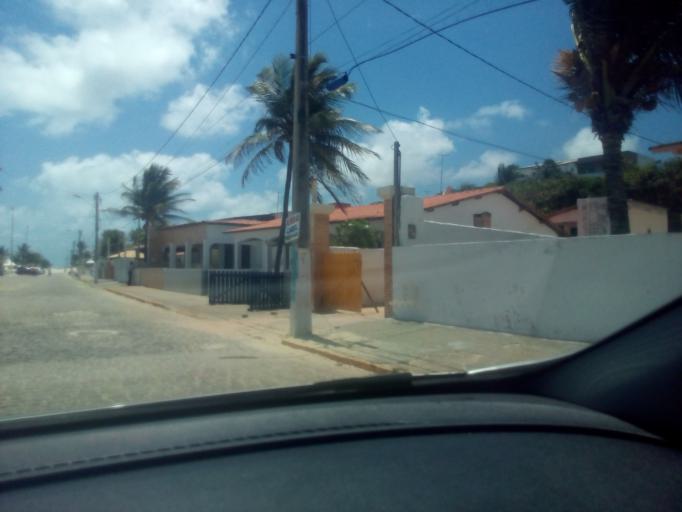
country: BR
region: Rio Grande do Norte
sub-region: Parnamirim
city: Parnamirim
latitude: -5.9699
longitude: -35.1279
